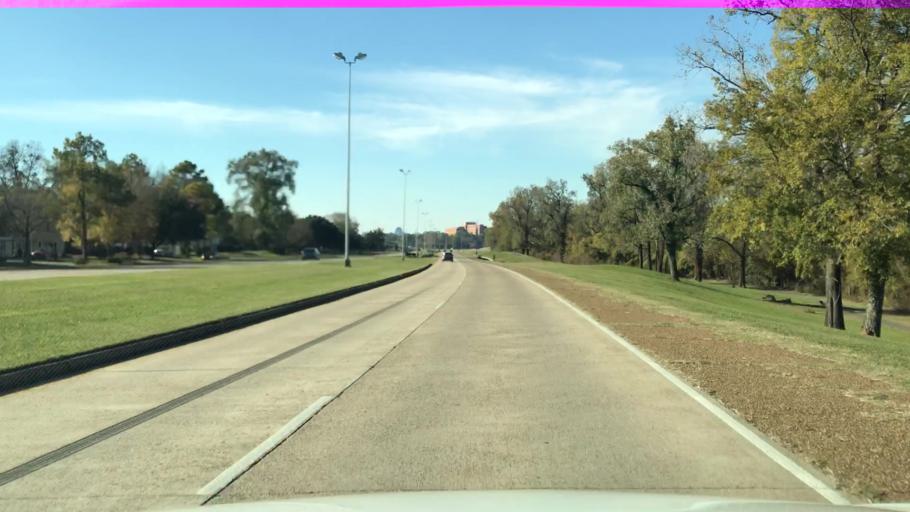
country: US
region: Louisiana
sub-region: Bossier Parish
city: Bossier City
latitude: 32.4925
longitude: -93.7030
